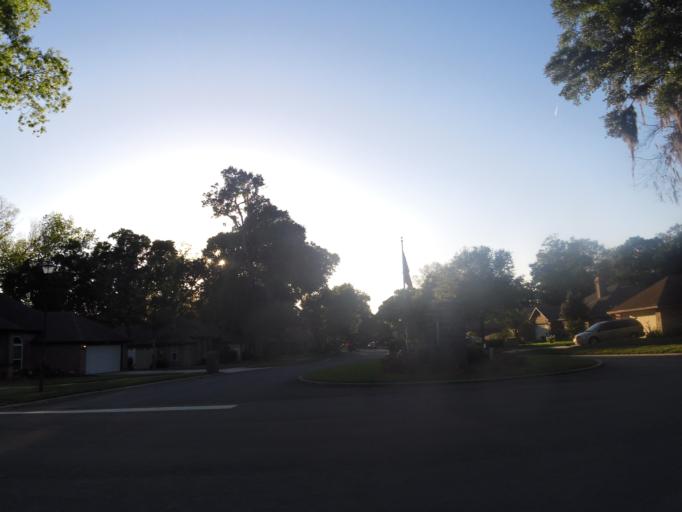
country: US
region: Florida
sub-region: Duval County
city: Atlantic Beach
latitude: 30.3597
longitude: -81.5164
